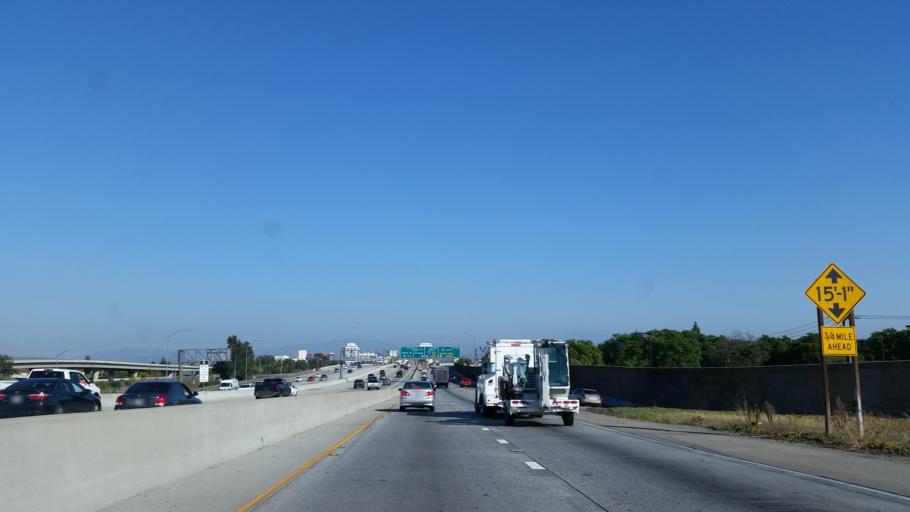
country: US
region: California
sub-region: Orange County
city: Orange
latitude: 33.7788
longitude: -117.8832
